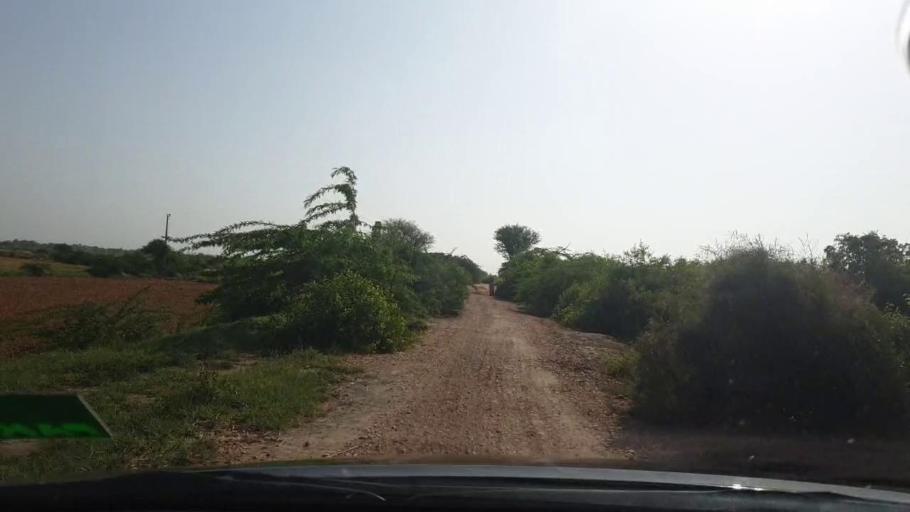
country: PK
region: Sindh
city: Tando Bago
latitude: 24.7126
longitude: 68.9815
